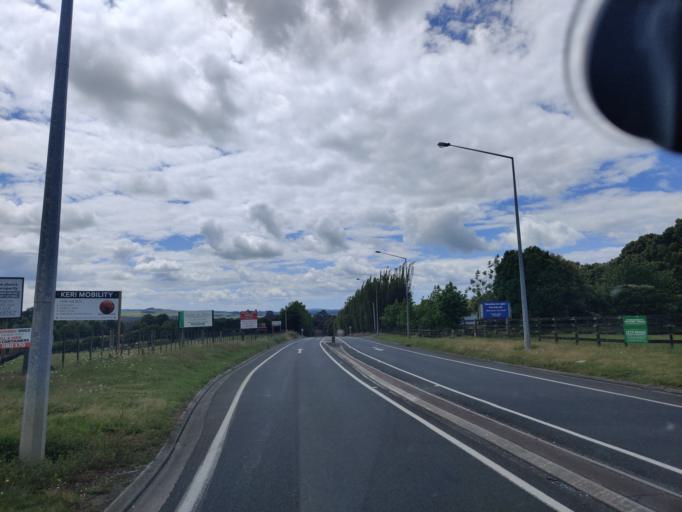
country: NZ
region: Northland
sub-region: Far North District
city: Kerikeri
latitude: -35.2535
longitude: 173.9317
